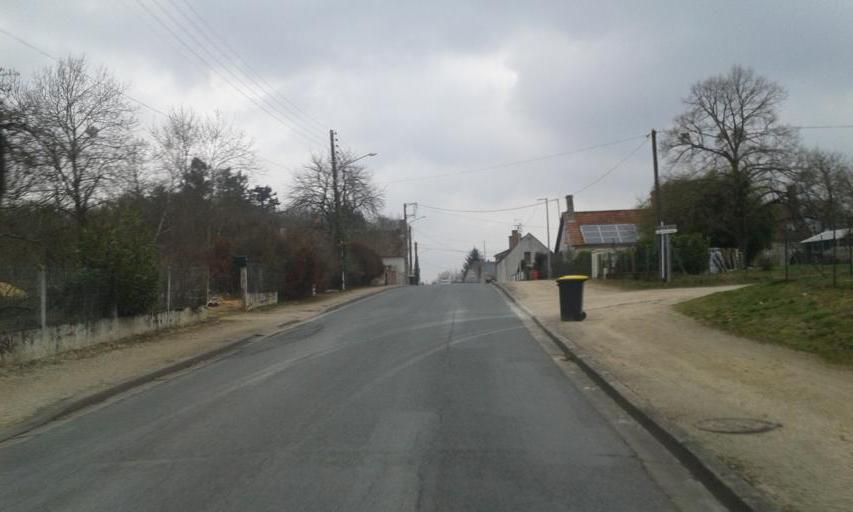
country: FR
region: Centre
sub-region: Departement du Loir-et-Cher
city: Dhuizon
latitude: 47.5914
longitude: 1.6586
